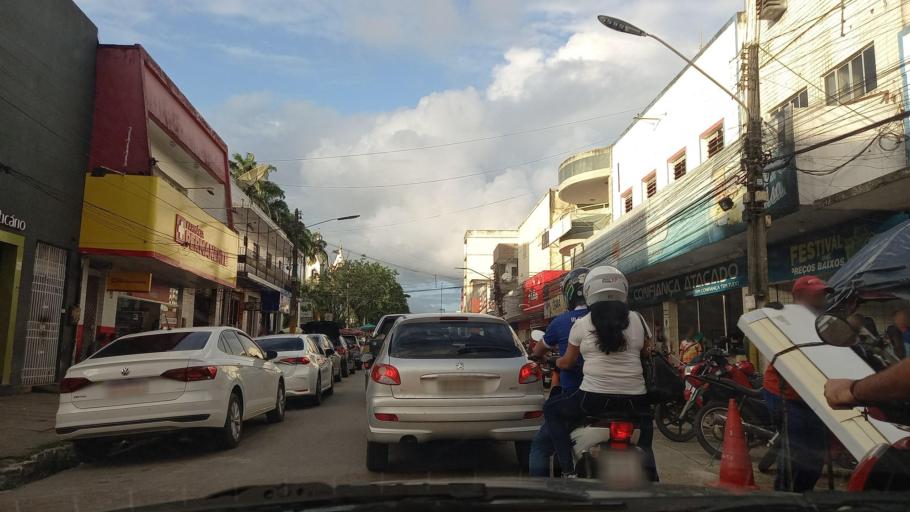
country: BR
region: Pernambuco
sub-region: Palmares
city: Palmares
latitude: -8.6865
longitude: -35.5909
